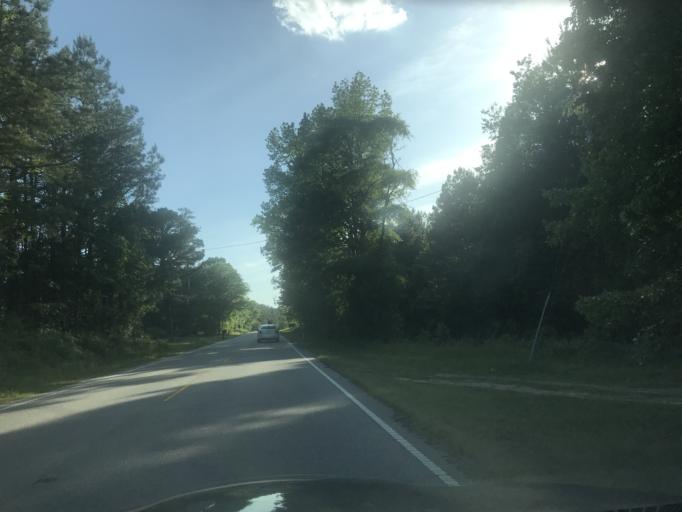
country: US
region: North Carolina
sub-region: Wake County
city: Knightdale
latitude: 35.7487
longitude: -78.4347
